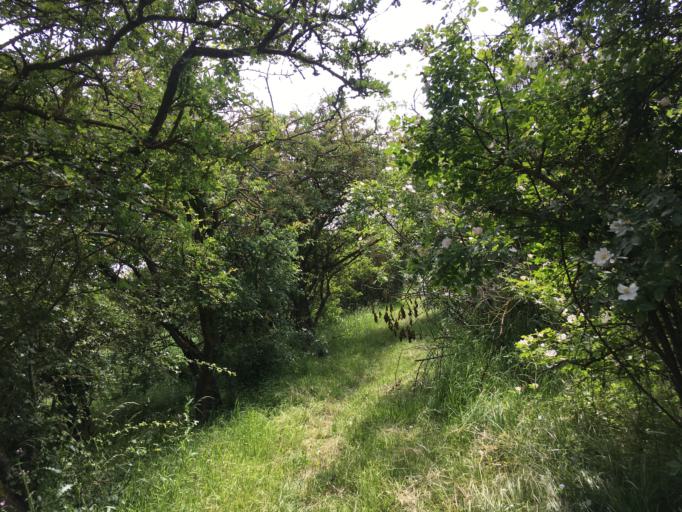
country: GB
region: England
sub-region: Kent
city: Queenborough
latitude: 51.3824
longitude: 0.7533
